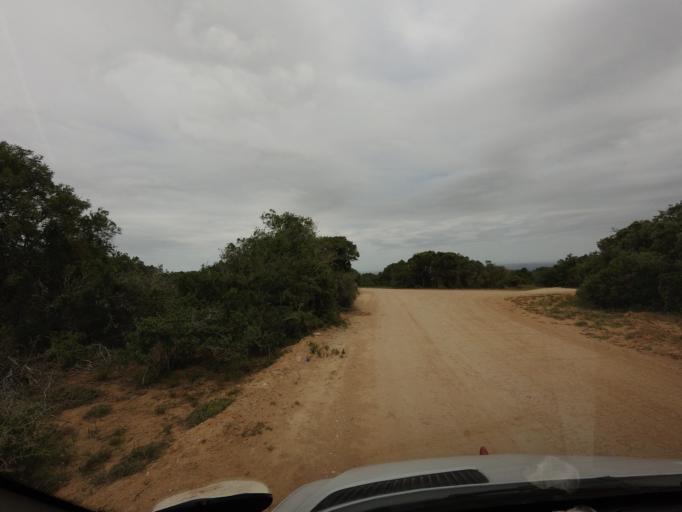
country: ZA
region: Eastern Cape
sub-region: Cacadu District Municipality
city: Kirkwood
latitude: -33.4905
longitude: 25.7627
